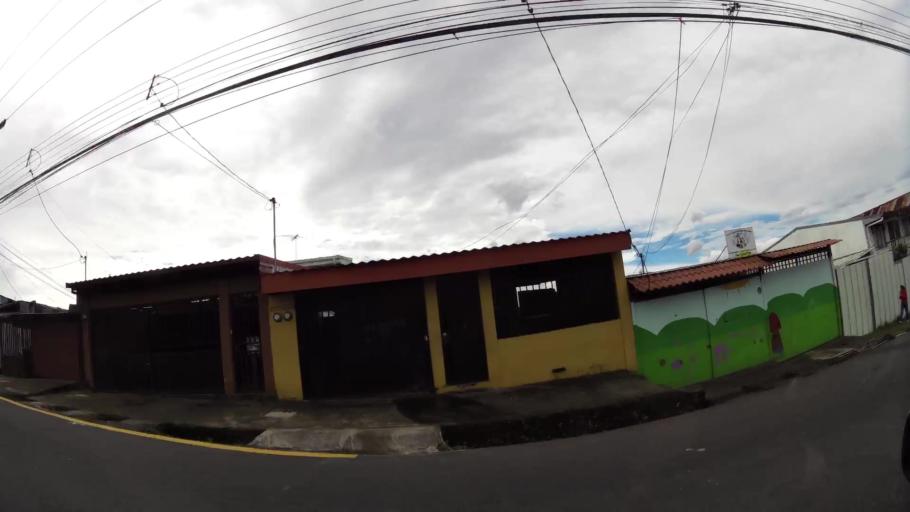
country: CR
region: San Jose
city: Purral
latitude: 9.9576
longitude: -84.0282
